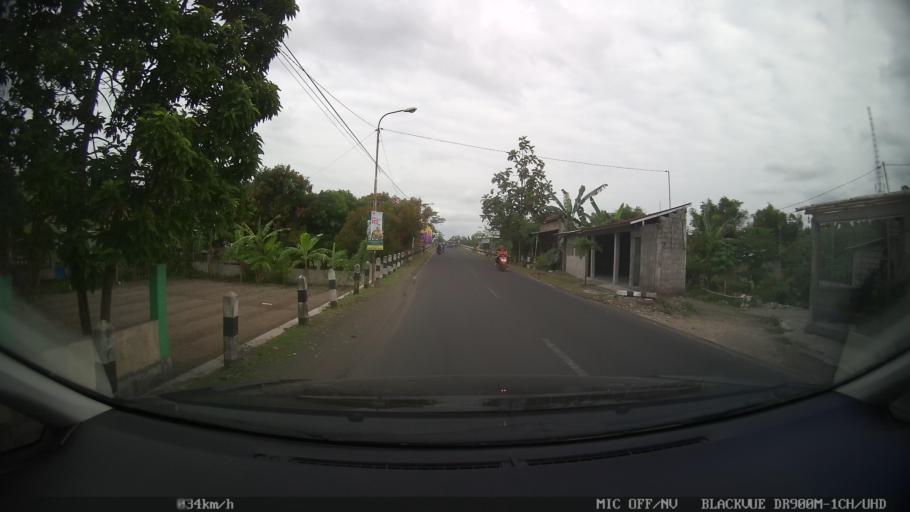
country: ID
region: Daerah Istimewa Yogyakarta
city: Depok
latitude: -7.8277
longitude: 110.4230
